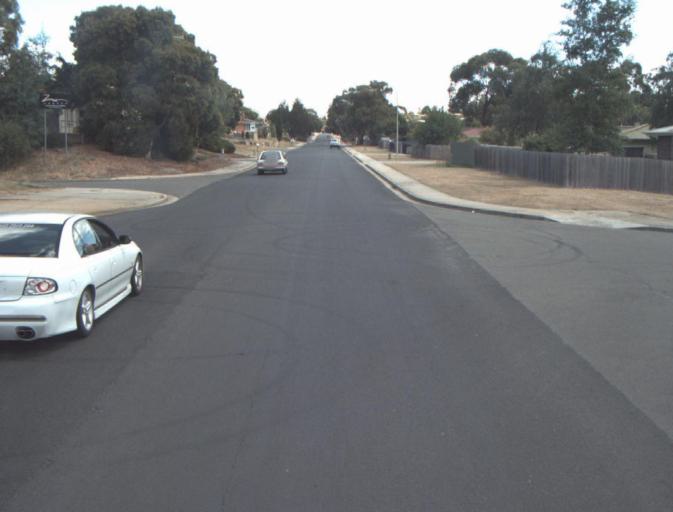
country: AU
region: Tasmania
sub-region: Launceston
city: Newstead
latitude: -41.4152
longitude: 147.1728
